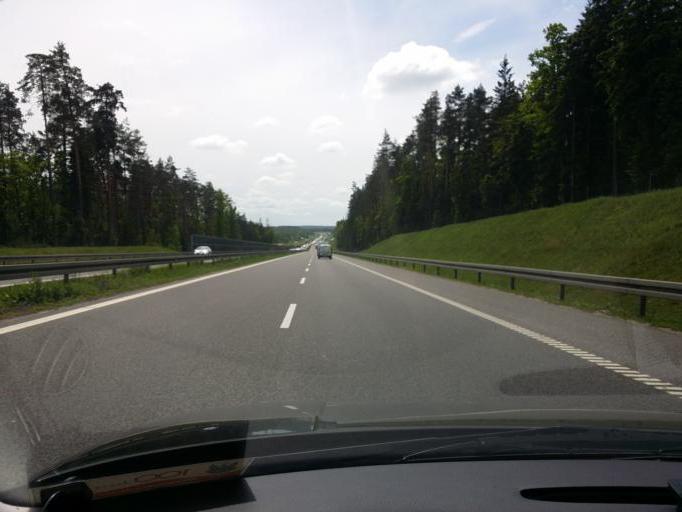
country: PL
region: Swietokrzyskie
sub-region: Powiat skarzyski
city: Suchedniow
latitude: 51.0669
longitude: 20.8339
